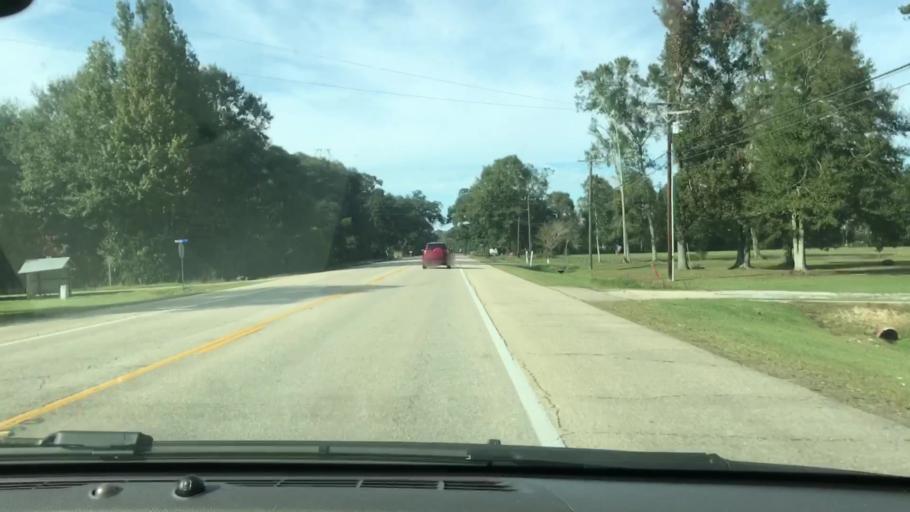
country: US
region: Louisiana
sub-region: Saint Tammany Parish
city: Pearl River
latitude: 30.4510
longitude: -89.8003
